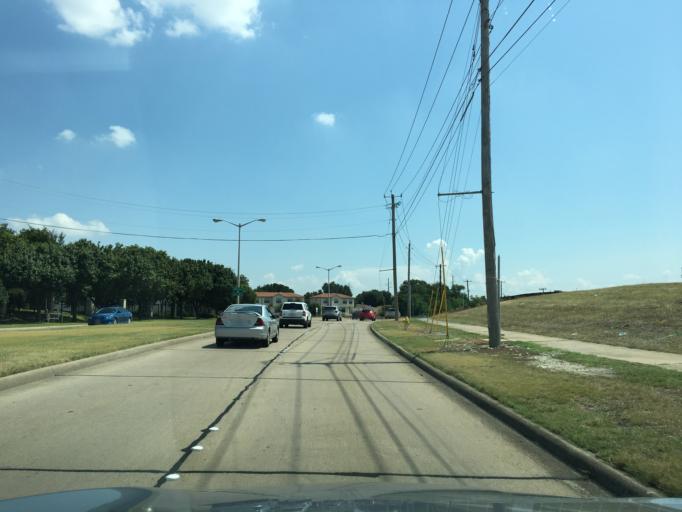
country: US
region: Texas
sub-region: Dallas County
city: Garland
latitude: 32.9481
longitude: -96.6494
